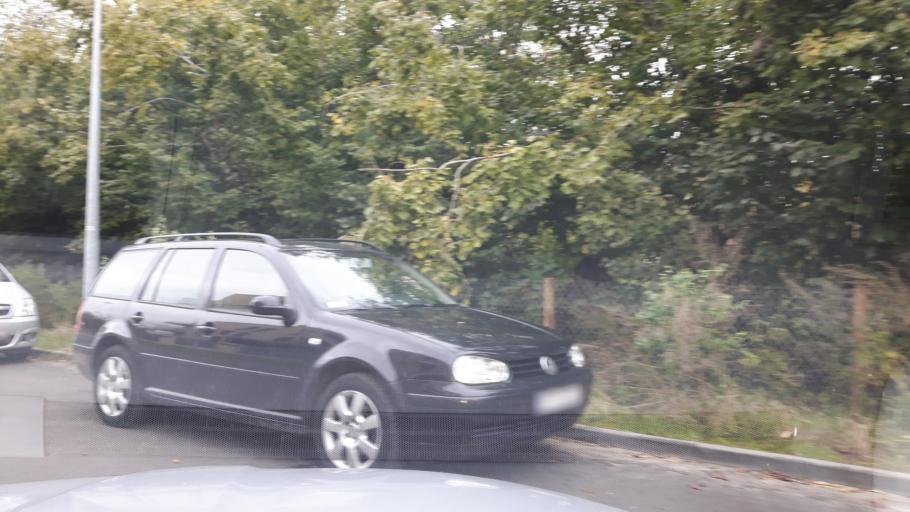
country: PL
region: Masovian Voivodeship
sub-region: Warszawa
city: Mokotow
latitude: 52.1777
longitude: 21.0380
